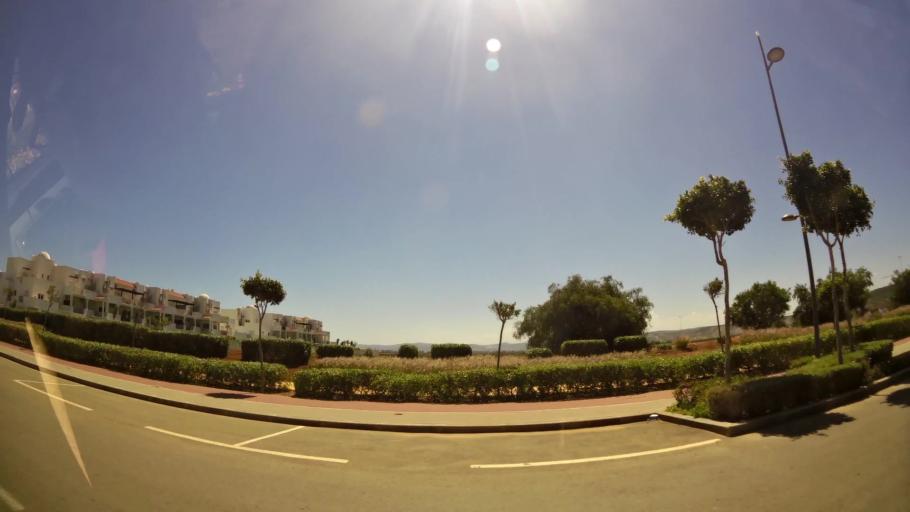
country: MA
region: Oriental
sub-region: Berkane-Taourirt
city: Madagh
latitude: 35.0979
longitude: -2.3007
